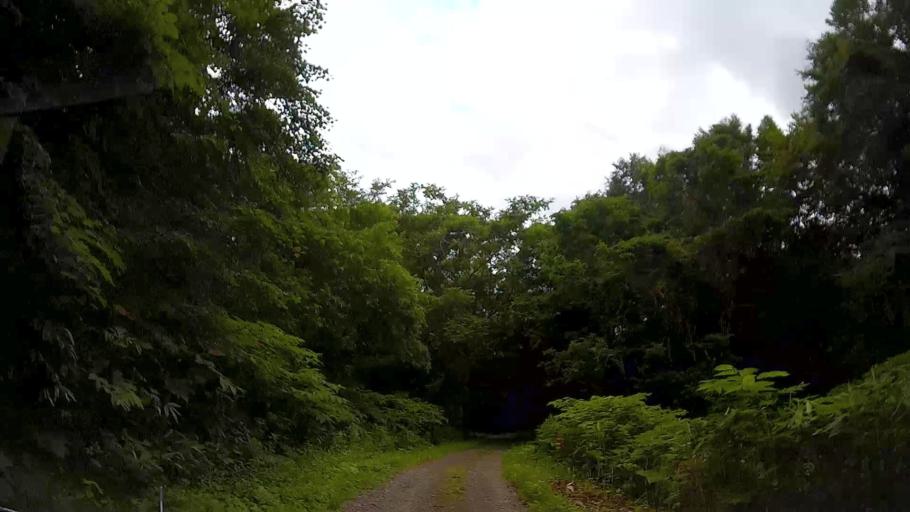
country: JP
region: Hokkaido
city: Nanae
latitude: 42.0414
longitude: 140.4861
